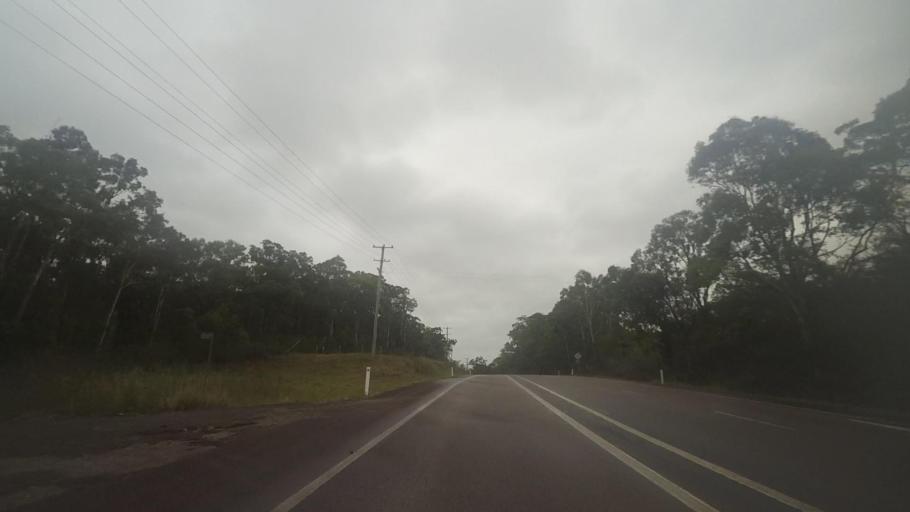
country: AU
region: New South Wales
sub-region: Port Stephens Shire
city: Port Stephens
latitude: -32.6435
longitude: 151.9858
